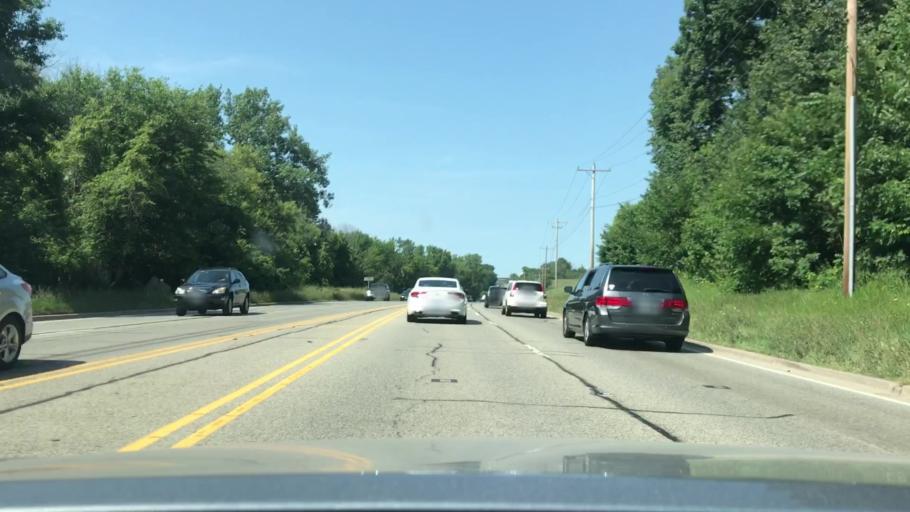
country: US
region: Illinois
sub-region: Kane County
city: Batavia
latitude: 41.8418
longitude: -88.2795
